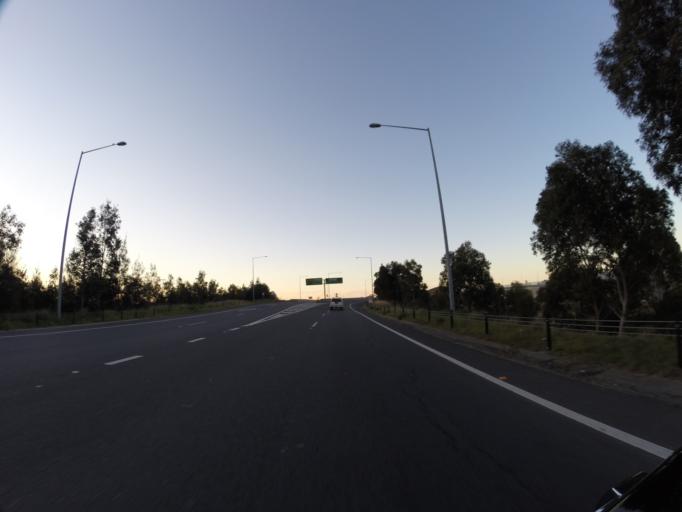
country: AU
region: New South Wales
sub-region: Campbelltown Municipality
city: Glenfield
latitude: -33.9554
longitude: 150.8760
